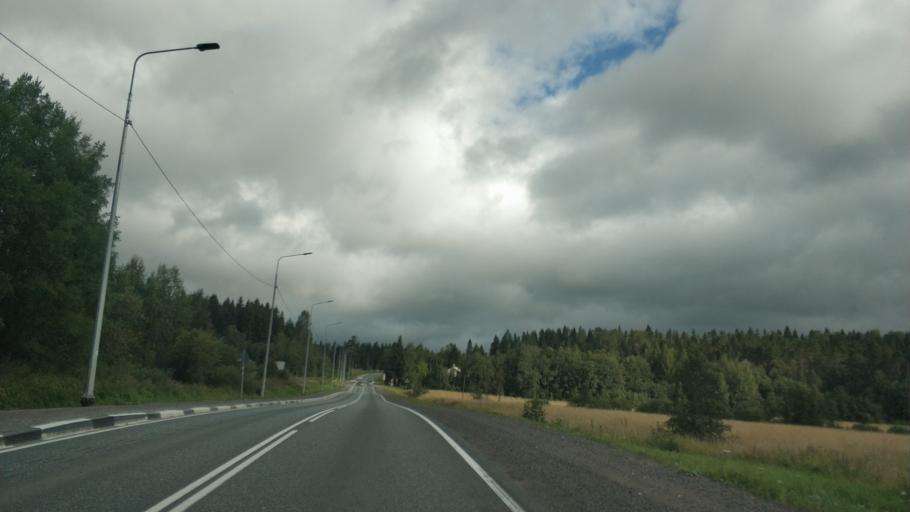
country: RU
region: Republic of Karelia
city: Khelyulya
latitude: 61.7640
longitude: 30.6559
